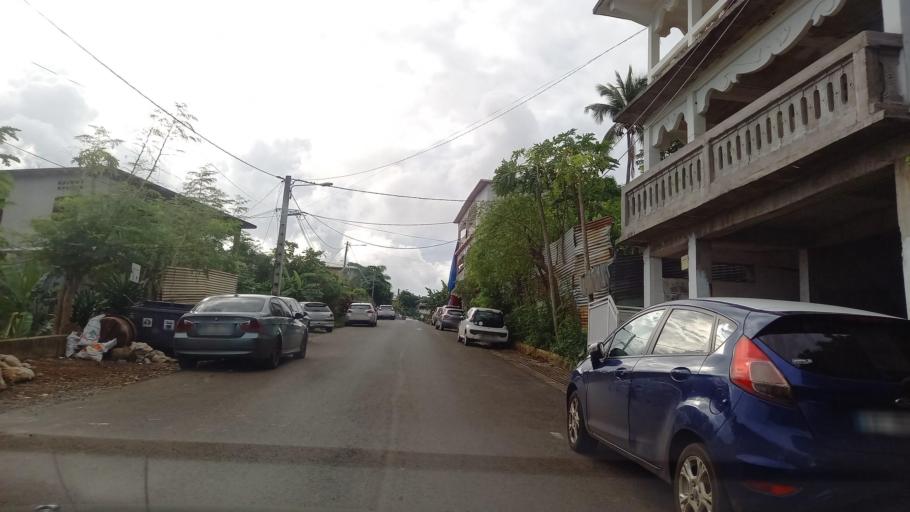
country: YT
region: Sada
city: Sada
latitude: -12.8539
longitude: 45.0987
